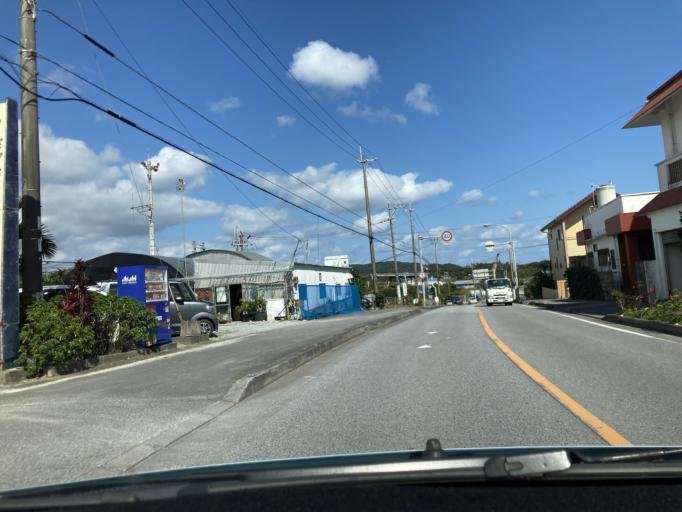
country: JP
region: Okinawa
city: Nago
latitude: 26.6128
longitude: 128.0006
